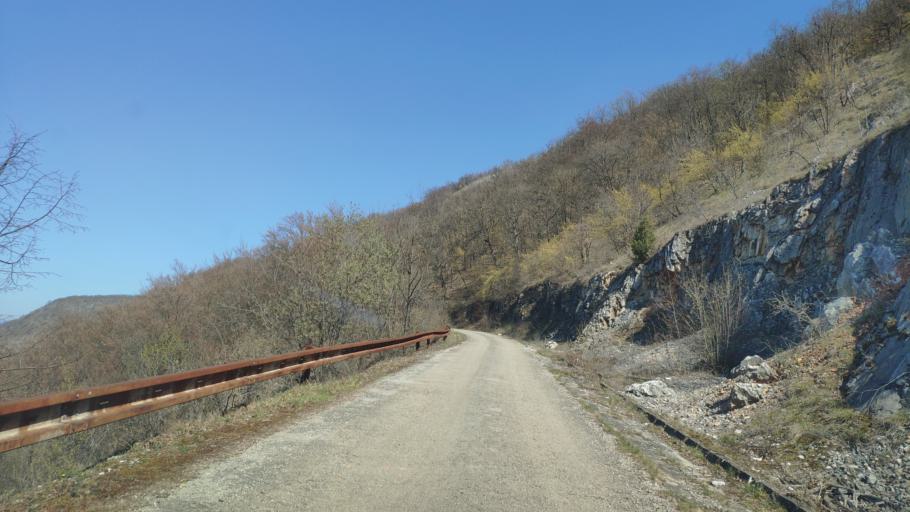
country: SK
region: Kosicky
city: Roznava
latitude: 48.5736
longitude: 20.4061
